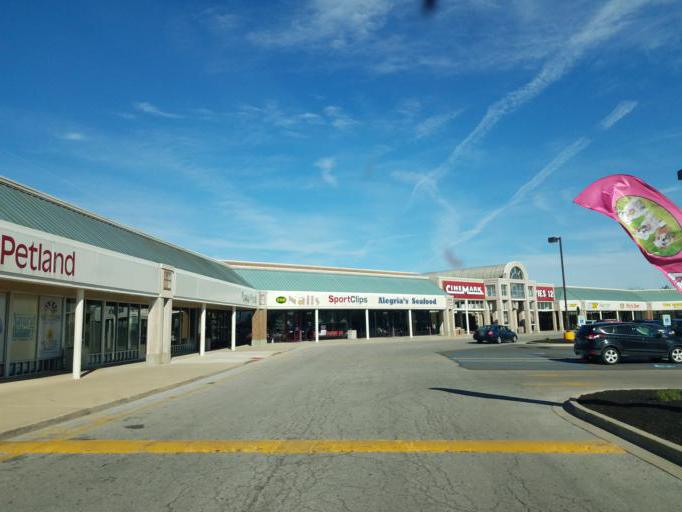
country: US
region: Ohio
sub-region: Franklin County
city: Dublin
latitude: 40.0669
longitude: -83.0882
